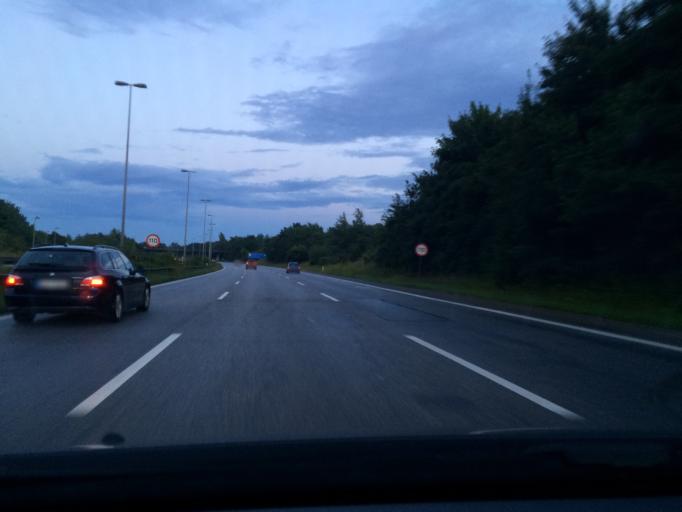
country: DK
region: Capital Region
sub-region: Brondby Kommune
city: Brondbyvester
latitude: 55.6209
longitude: 12.4424
